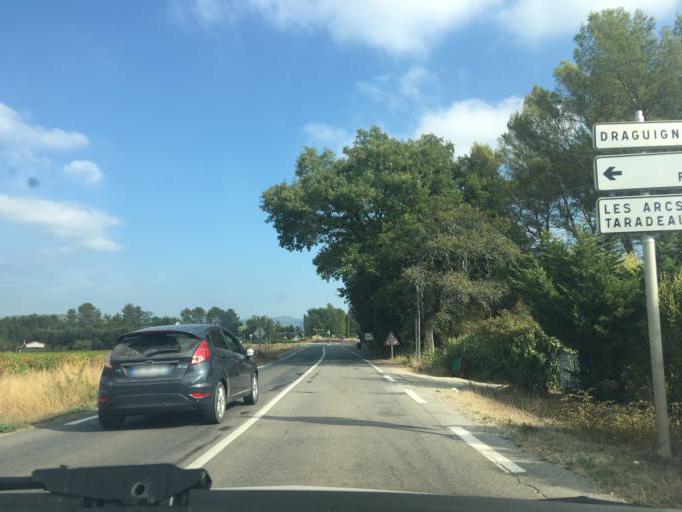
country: FR
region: Provence-Alpes-Cote d'Azur
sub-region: Departement du Var
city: Flayosc
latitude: 43.5086
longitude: 6.4246
